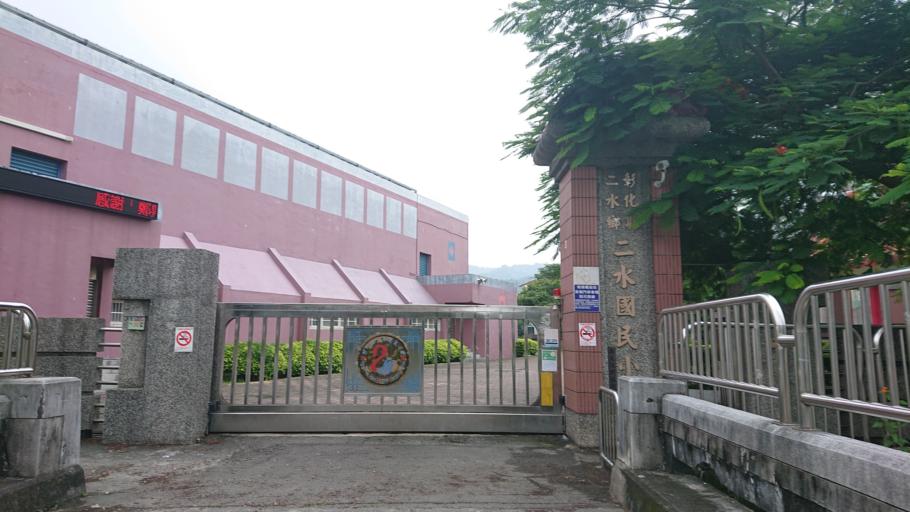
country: TW
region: Taiwan
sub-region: Nantou
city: Nantou
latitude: 23.8105
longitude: 120.6172
